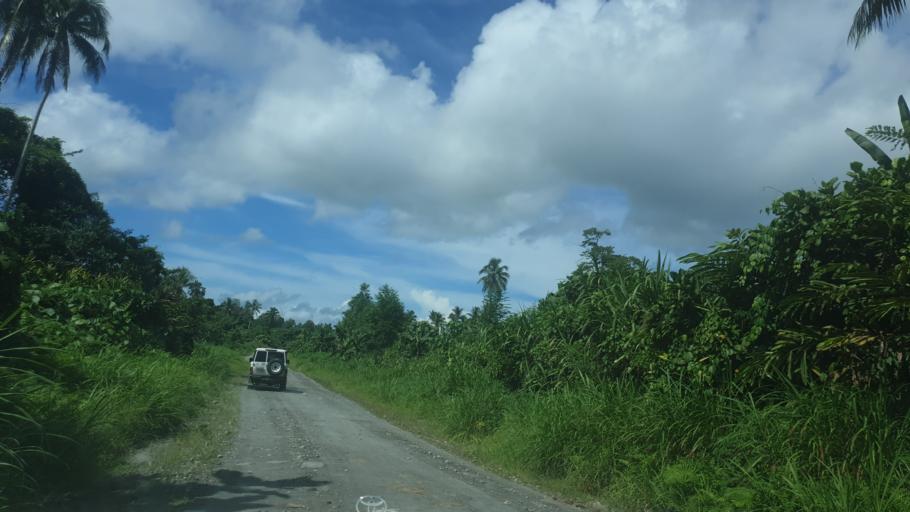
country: PG
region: Bougainville
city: Panguna
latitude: -6.5595
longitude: 155.3546
